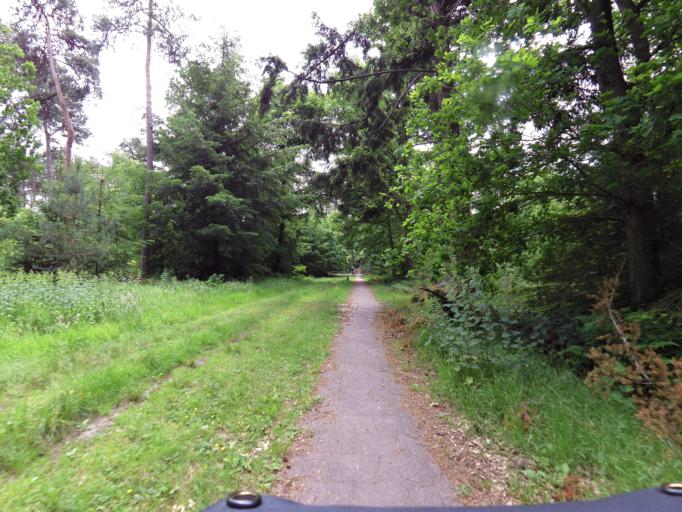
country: NL
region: North Brabant
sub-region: Gemeente Baarle-Nassau
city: Baarle-Nassau
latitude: 51.5027
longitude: 4.9097
